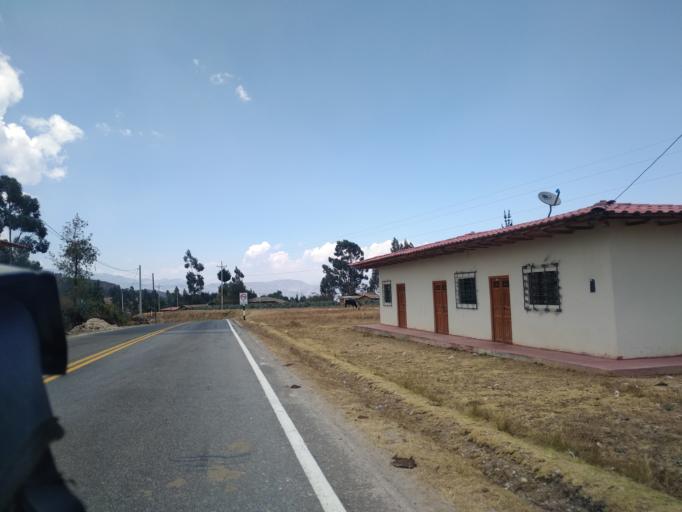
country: PE
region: Cajamarca
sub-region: San Marcos
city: San Marcos
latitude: -7.2823
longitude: -78.2267
